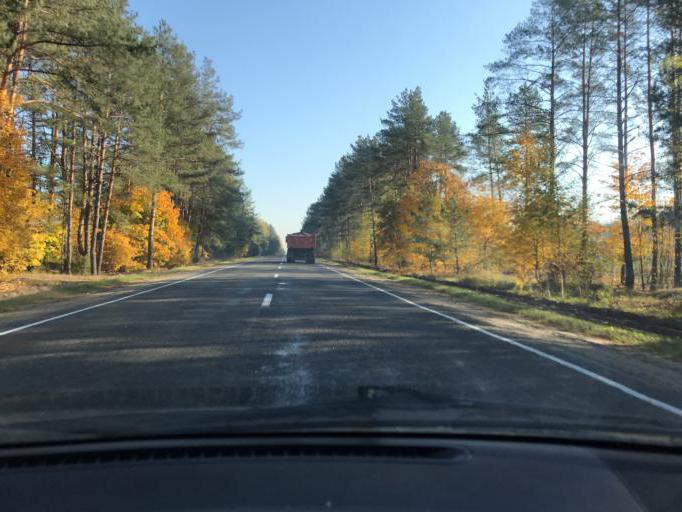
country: BY
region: Brest
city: Baranovichi
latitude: 52.9114
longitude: 25.9307
